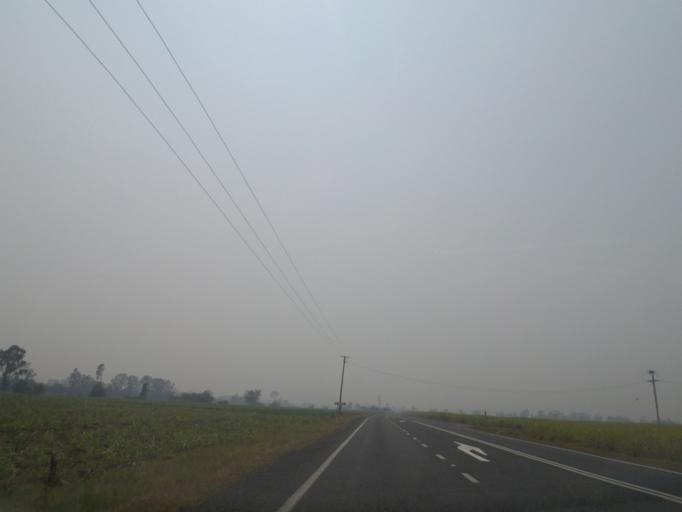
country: AU
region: New South Wales
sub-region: Clarence Valley
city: Maclean
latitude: -29.5645
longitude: 153.1109
